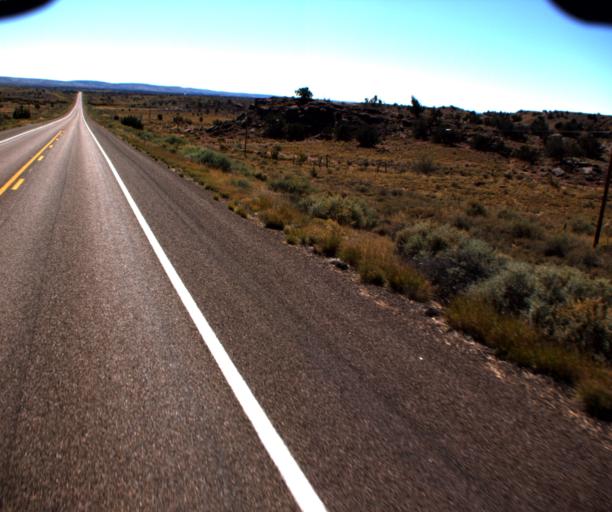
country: US
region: Arizona
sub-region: Apache County
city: Saint Johns
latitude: 34.6361
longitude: -109.6863
